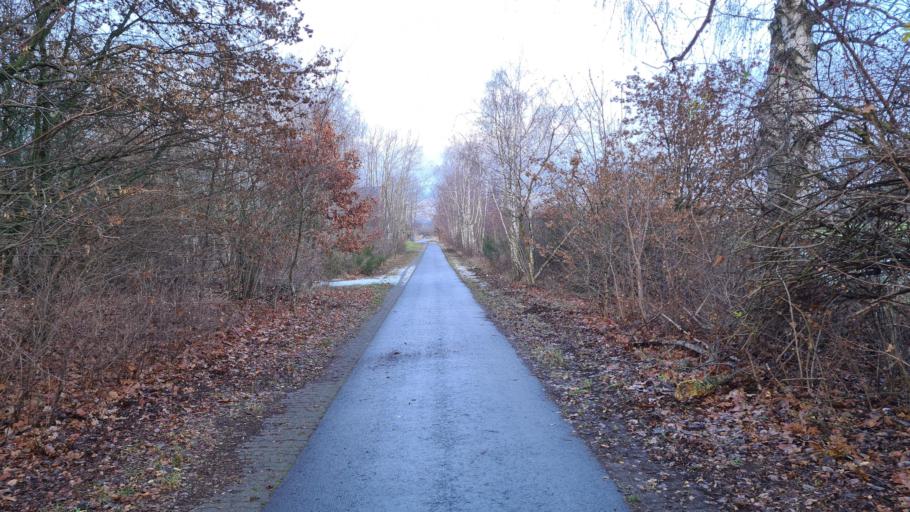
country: DE
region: Brandenburg
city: Groden
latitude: 51.3993
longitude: 13.5827
